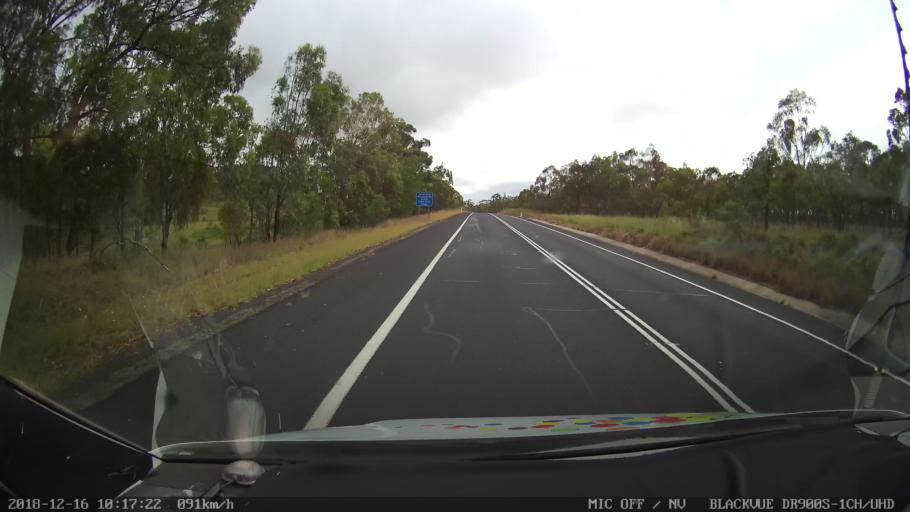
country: AU
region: New South Wales
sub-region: Tenterfield Municipality
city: Carrolls Creek
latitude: -29.2566
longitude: 151.9911
